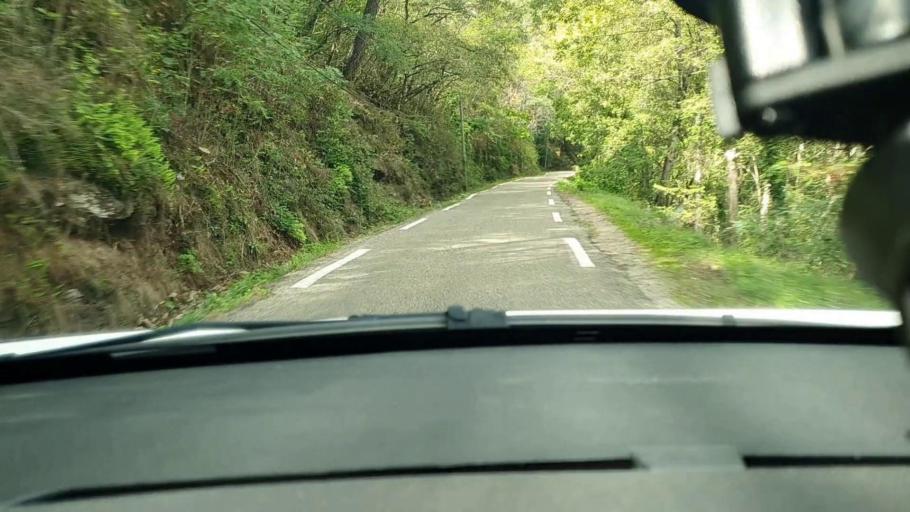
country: FR
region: Languedoc-Roussillon
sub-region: Departement du Gard
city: Besseges
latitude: 44.2999
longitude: 4.0250
